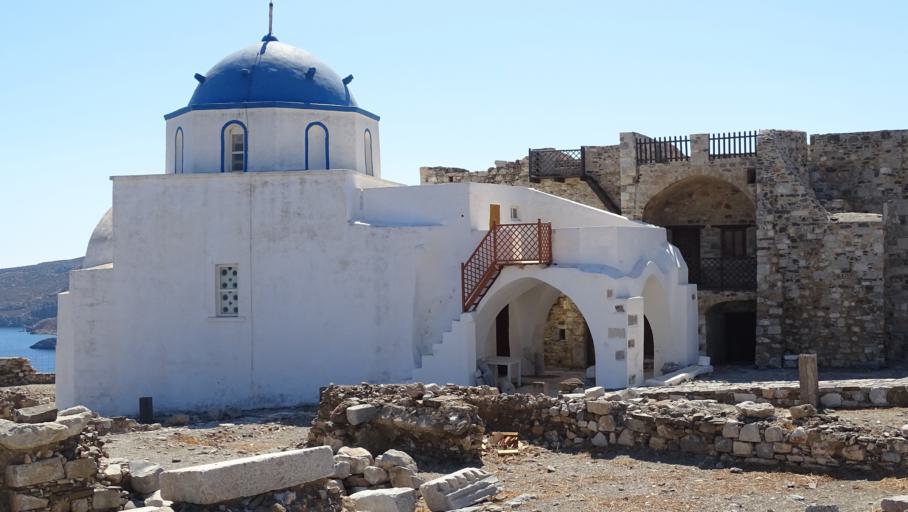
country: GR
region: South Aegean
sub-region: Nomos Dodekanisou
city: Astypalaia
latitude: 36.5443
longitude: 26.3554
